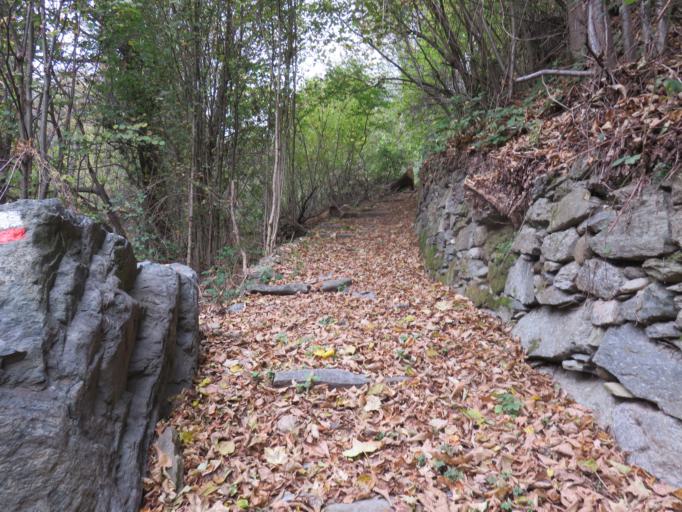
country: IT
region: Piedmont
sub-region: Provincia di Torino
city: Ceres
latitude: 45.3255
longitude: 7.3956
